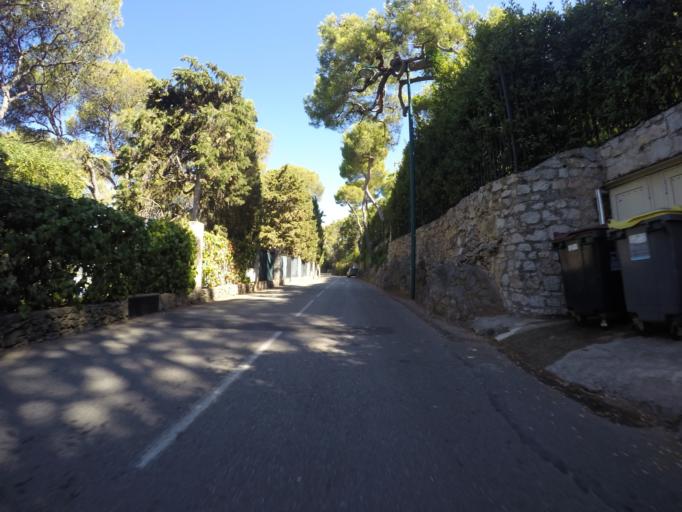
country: FR
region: Provence-Alpes-Cote d'Azur
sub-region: Departement des Alpes-Maritimes
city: Saint-Jean-Cap-Ferrat
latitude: 43.6808
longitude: 7.3263
